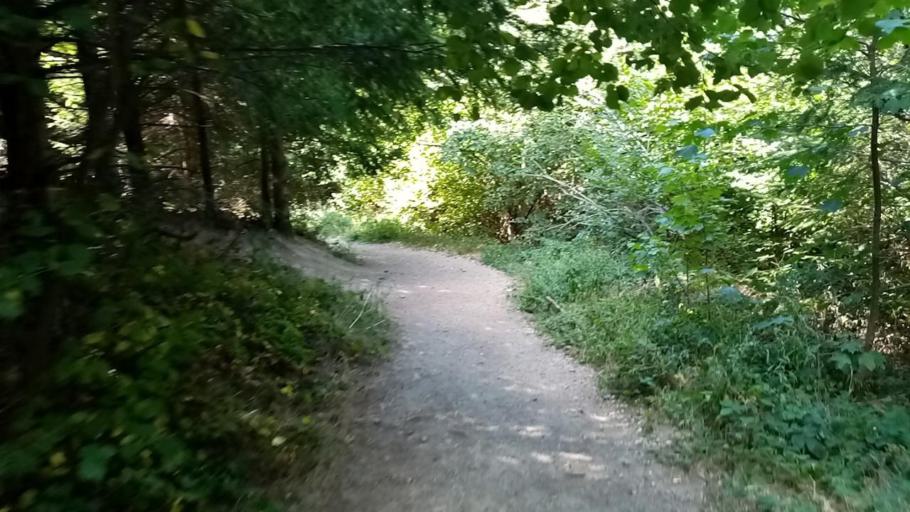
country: FR
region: Rhone-Alpes
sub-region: Departement du Rhone
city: Grandris
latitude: 46.0149
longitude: 4.5445
